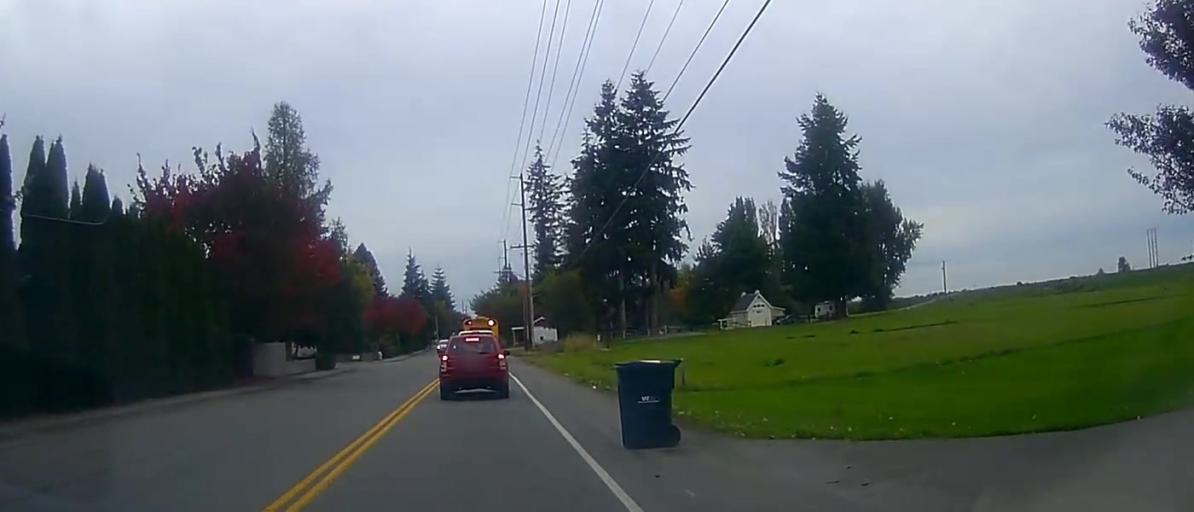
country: US
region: Washington
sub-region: Skagit County
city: Mount Vernon
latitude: 48.4431
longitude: -122.3269
